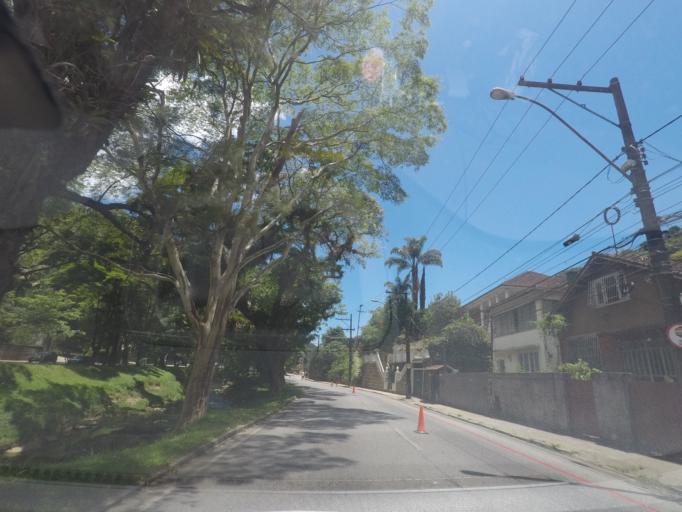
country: BR
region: Rio de Janeiro
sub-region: Petropolis
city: Petropolis
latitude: -22.4961
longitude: -43.1798
